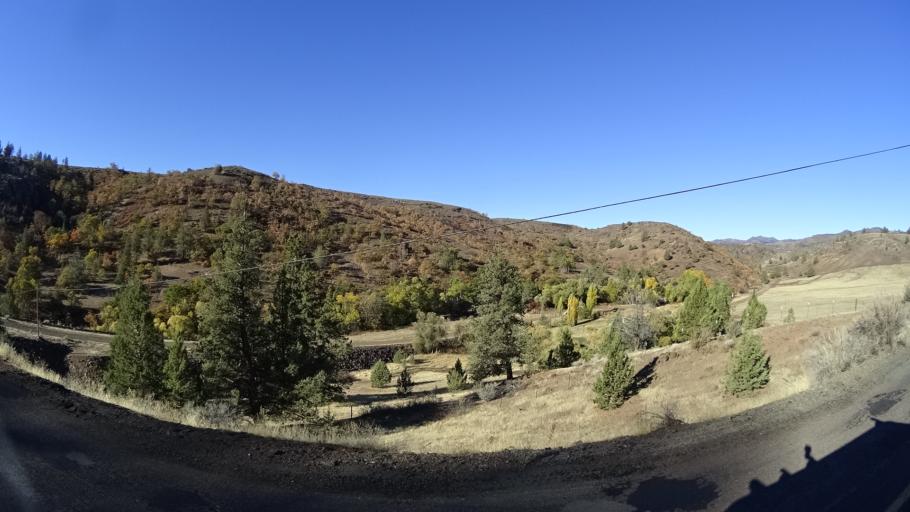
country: US
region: California
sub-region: Siskiyou County
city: Montague
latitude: 41.9382
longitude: -122.4450
